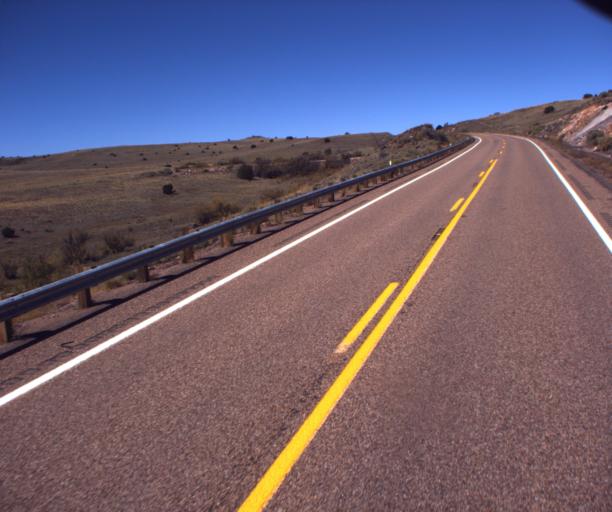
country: US
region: Arizona
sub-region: Apache County
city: Saint Johns
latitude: 34.5543
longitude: -109.4912
